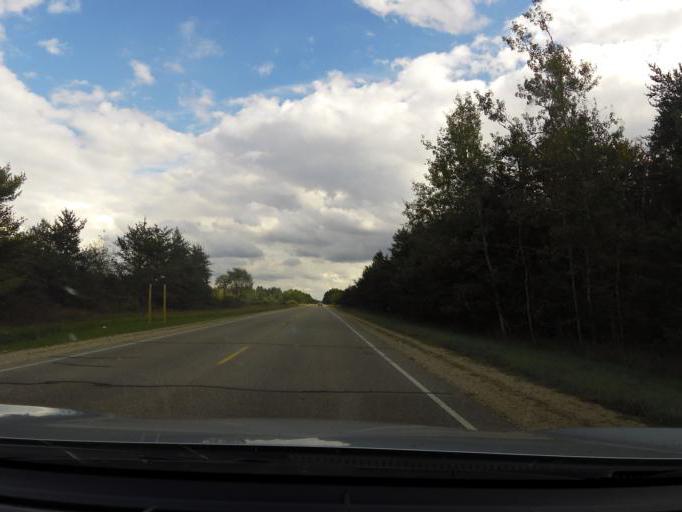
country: US
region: Michigan
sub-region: Roscommon County
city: Saint Helen
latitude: 44.4211
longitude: -84.4817
